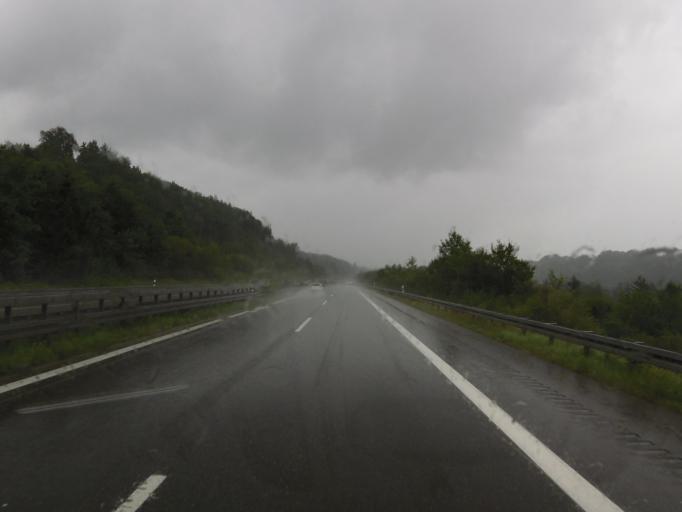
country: DE
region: Baden-Wuerttemberg
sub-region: Tuebingen Region
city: Wangen im Allgau
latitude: 47.7151
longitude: 9.8355
